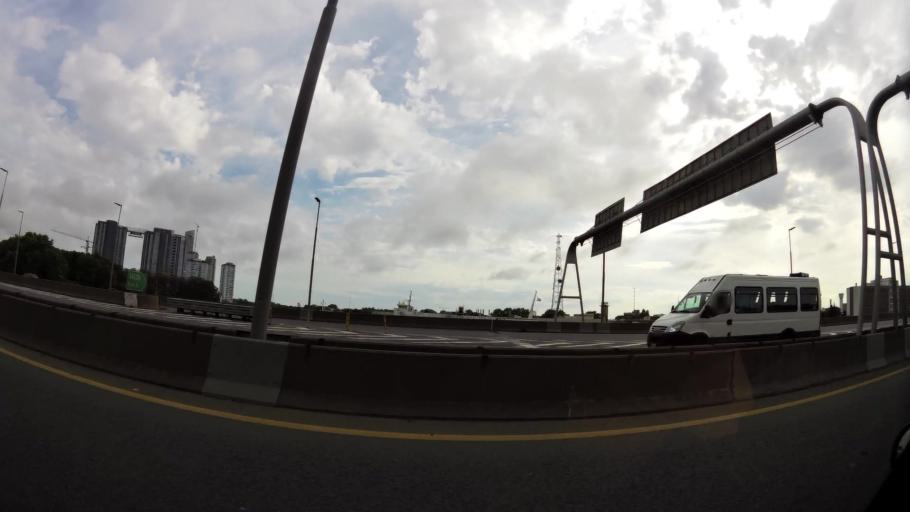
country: AR
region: Buenos Aires F.D.
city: Buenos Aires
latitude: -34.6253
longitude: -58.3607
